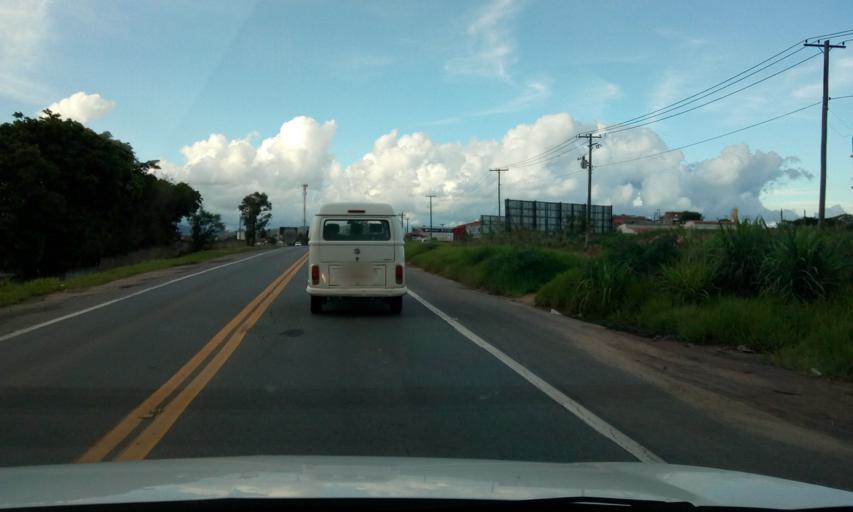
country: BR
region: Sao Paulo
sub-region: Itatiba
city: Itatiba
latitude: -23.0104
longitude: -46.8194
